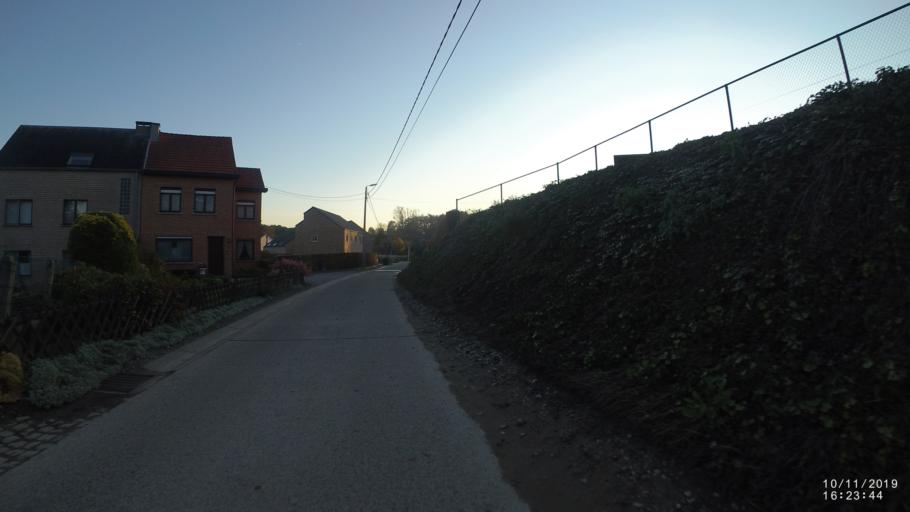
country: BE
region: Flanders
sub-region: Provincie Vlaams-Brabant
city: Lubbeek
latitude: 50.8785
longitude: 4.8333
